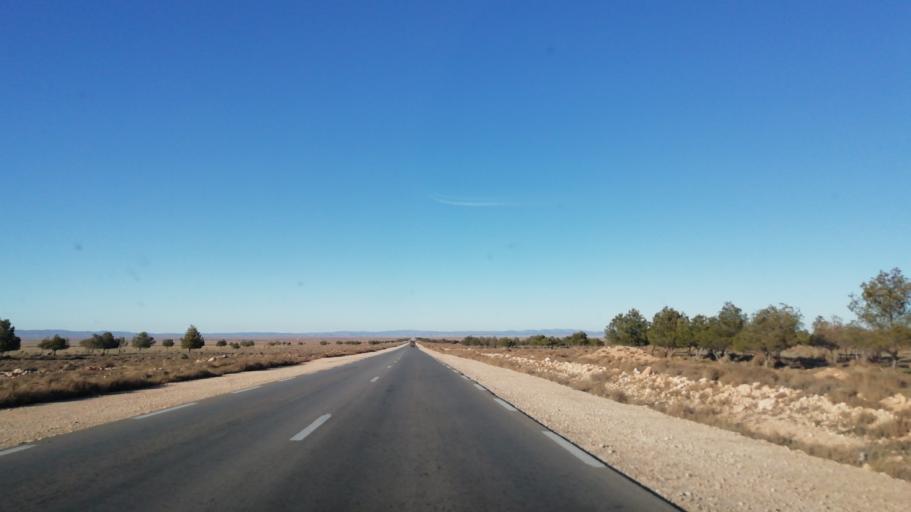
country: DZ
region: Tlemcen
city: Sebdou
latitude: 34.3246
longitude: -1.2636
